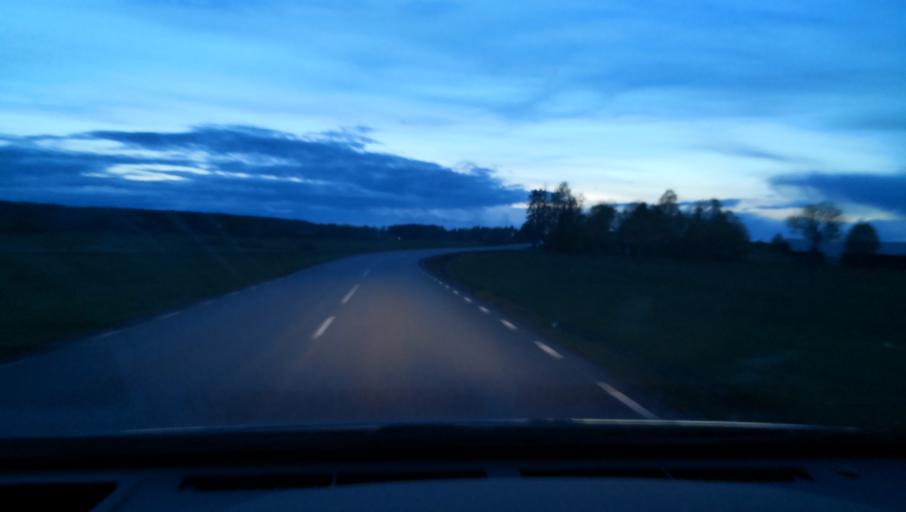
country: SE
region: OErebro
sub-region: Hallsbergs Kommun
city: Hallsberg
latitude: 59.1206
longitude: 15.0004
